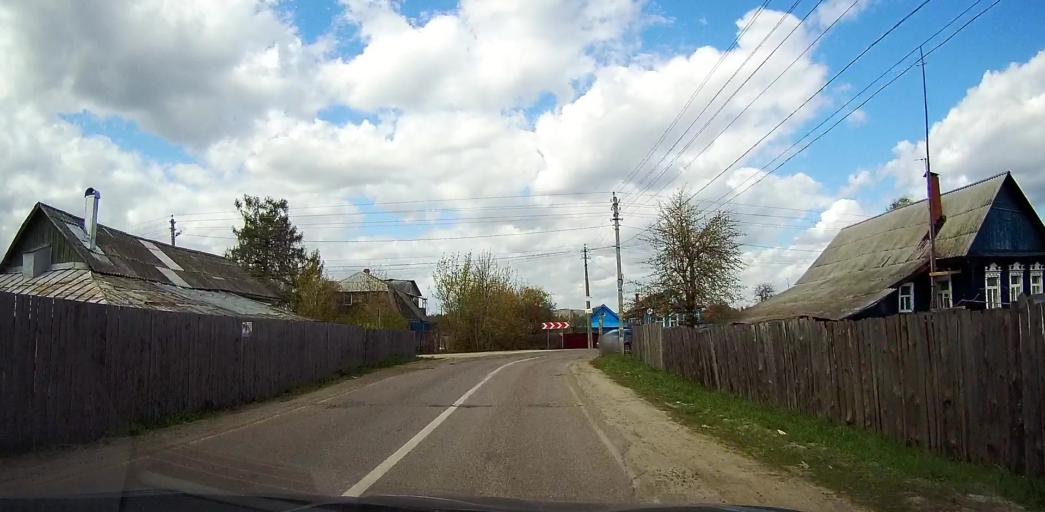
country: RU
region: Moskovskaya
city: Davydovo
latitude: 55.6045
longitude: 38.8466
